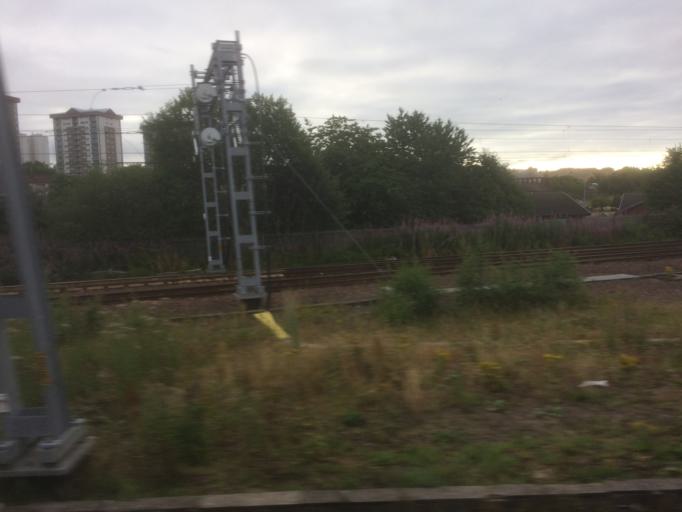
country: GB
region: Scotland
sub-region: Glasgow City
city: Glasgow
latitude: 55.8857
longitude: -4.2396
